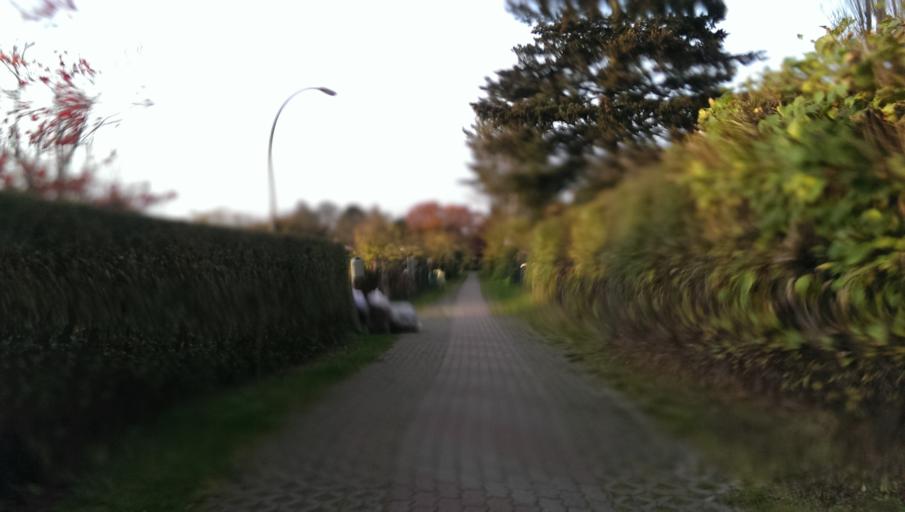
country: DE
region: Berlin
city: Lichterfelde
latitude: 52.4278
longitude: 13.2883
